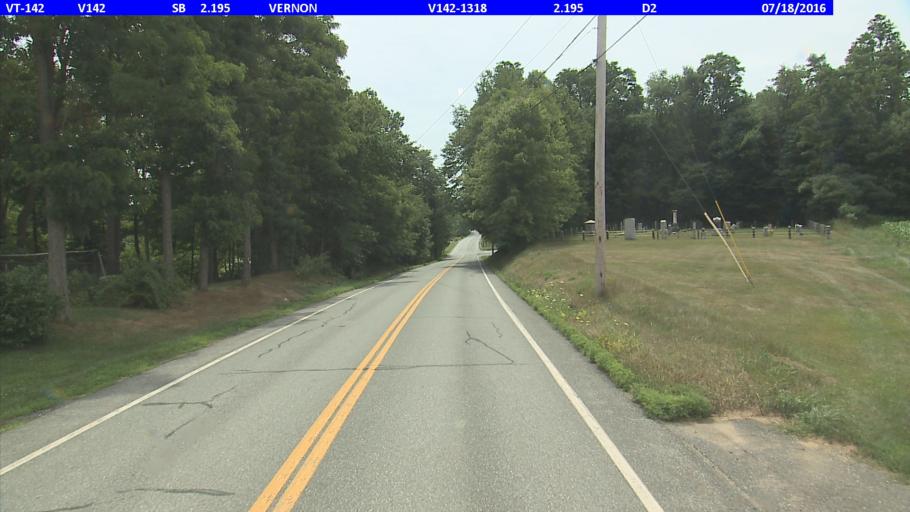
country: US
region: New Hampshire
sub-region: Cheshire County
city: Hinsdale
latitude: 42.7545
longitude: -72.4841
